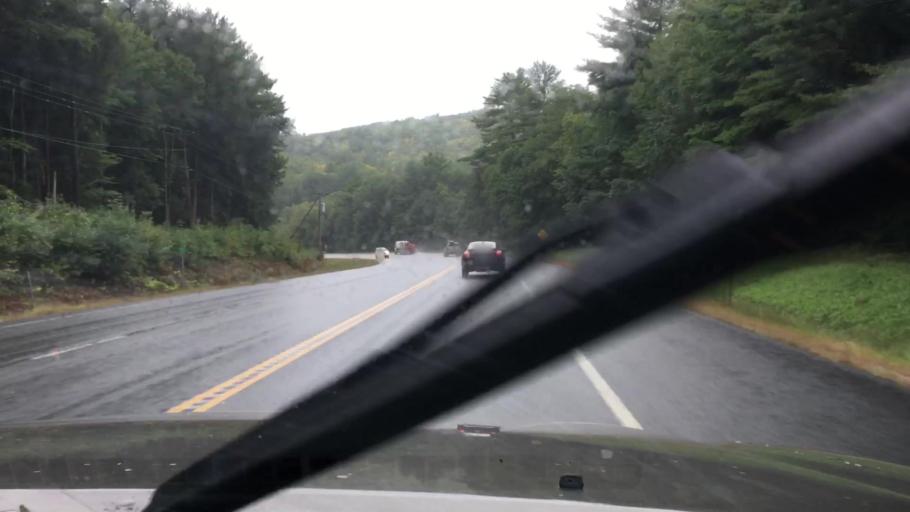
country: US
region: New Hampshire
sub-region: Cheshire County
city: Keene
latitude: 42.9684
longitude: -72.2555
